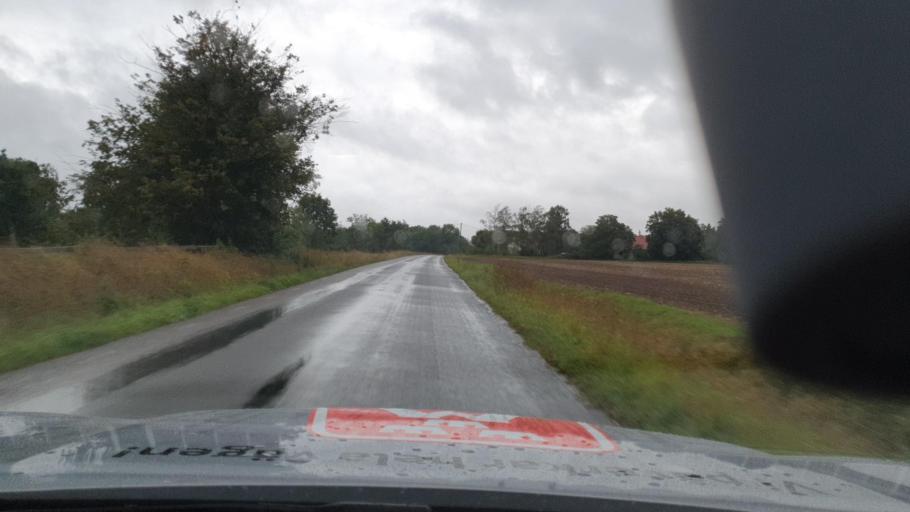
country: SE
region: Gotland
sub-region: Gotland
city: Visby
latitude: 57.7620
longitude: 18.4895
